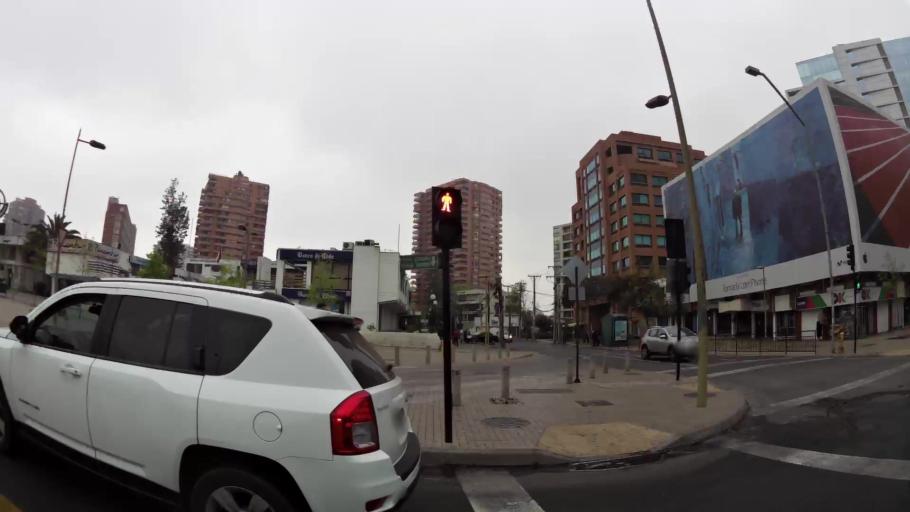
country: CL
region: Santiago Metropolitan
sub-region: Provincia de Santiago
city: Villa Presidente Frei, Nunoa, Santiago, Chile
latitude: -33.4097
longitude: -70.5704
